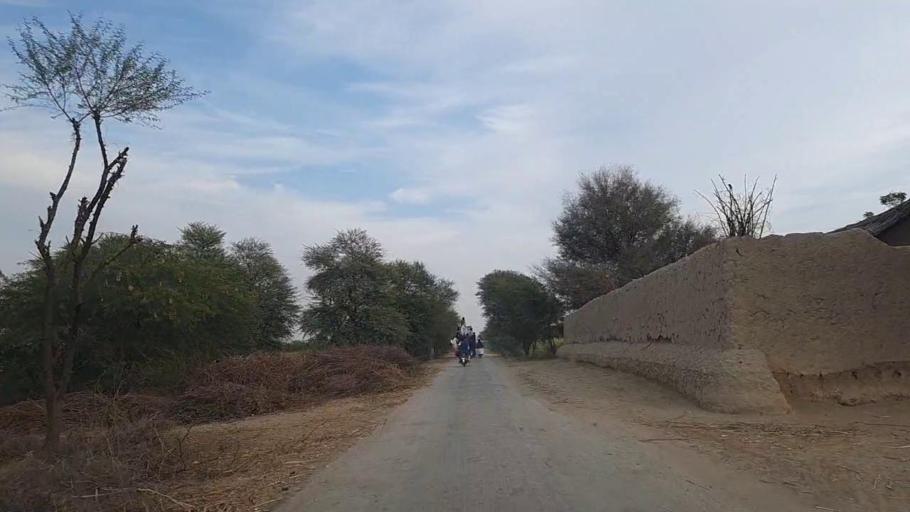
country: PK
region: Sindh
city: Daur
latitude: 26.5269
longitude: 68.4095
